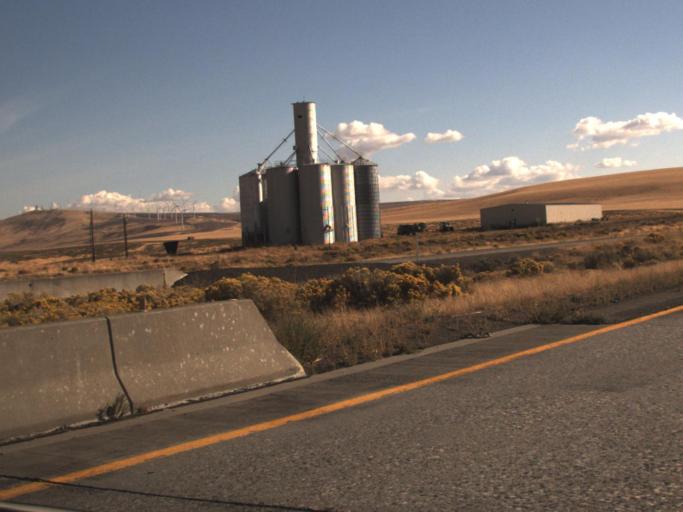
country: US
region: Washington
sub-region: Benton County
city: Highland
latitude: 46.1419
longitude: -119.2023
